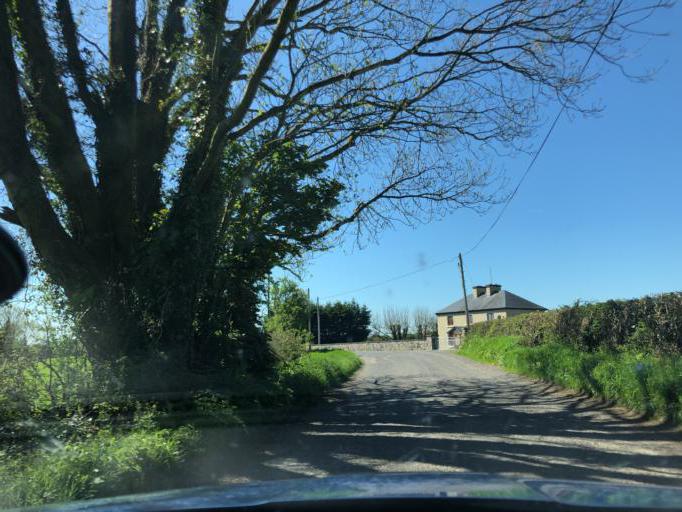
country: IE
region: Connaught
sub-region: County Galway
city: Portumna
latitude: 53.1494
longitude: -8.3392
